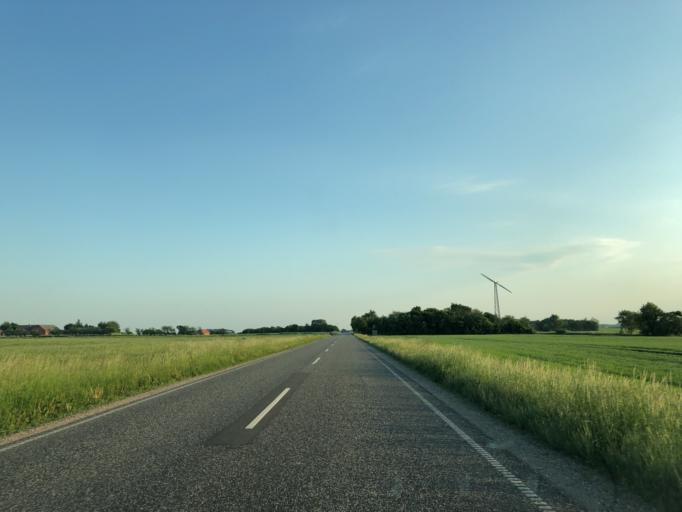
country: DK
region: Central Jutland
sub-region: Struer Kommune
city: Struer
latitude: 56.4511
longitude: 8.5377
